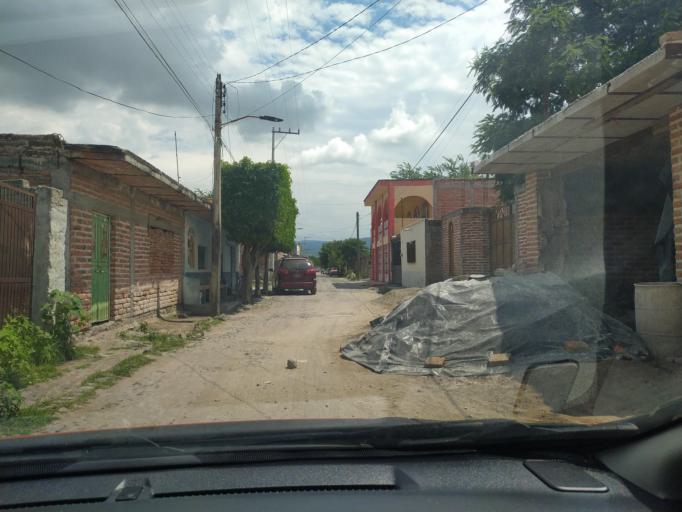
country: MX
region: Jalisco
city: Villa Corona
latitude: 20.3479
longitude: -103.6715
